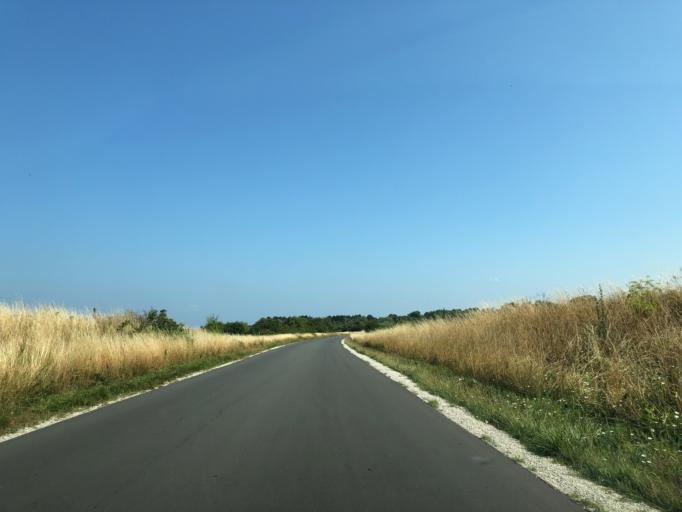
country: DK
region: Capital Region
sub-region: Halsnaes Kommune
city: Hundested
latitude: 55.9792
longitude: 11.8848
